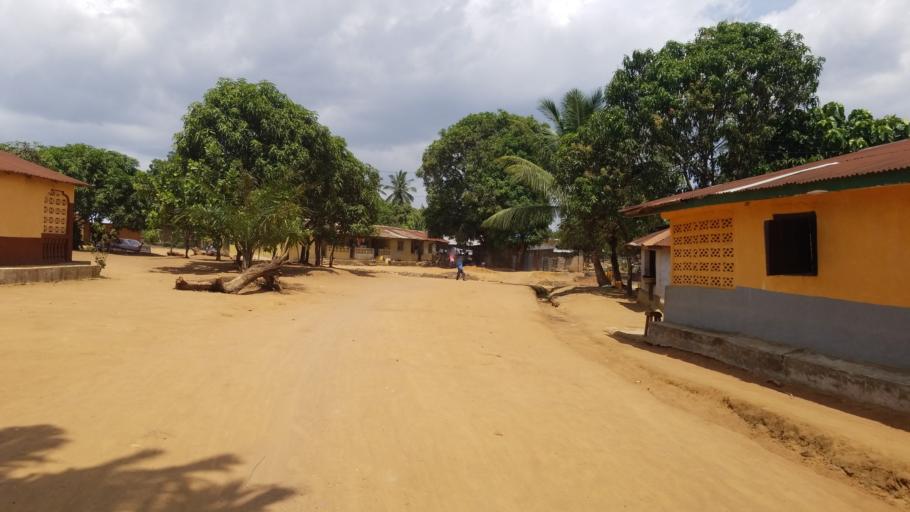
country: SL
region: Western Area
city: Waterloo
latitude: 8.3293
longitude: -13.0588
